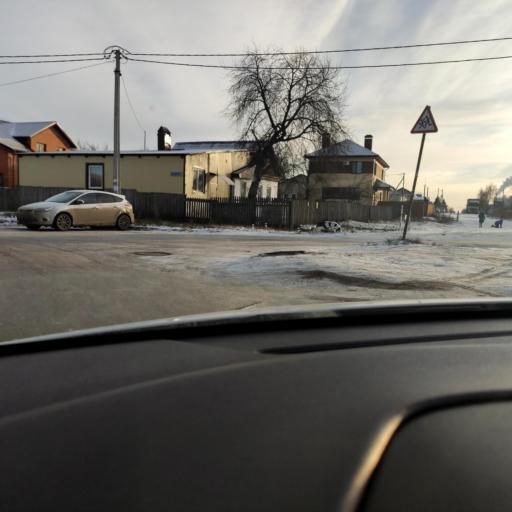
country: RU
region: Tatarstan
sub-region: Gorod Kazan'
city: Kazan
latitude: 55.8718
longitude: 49.0667
